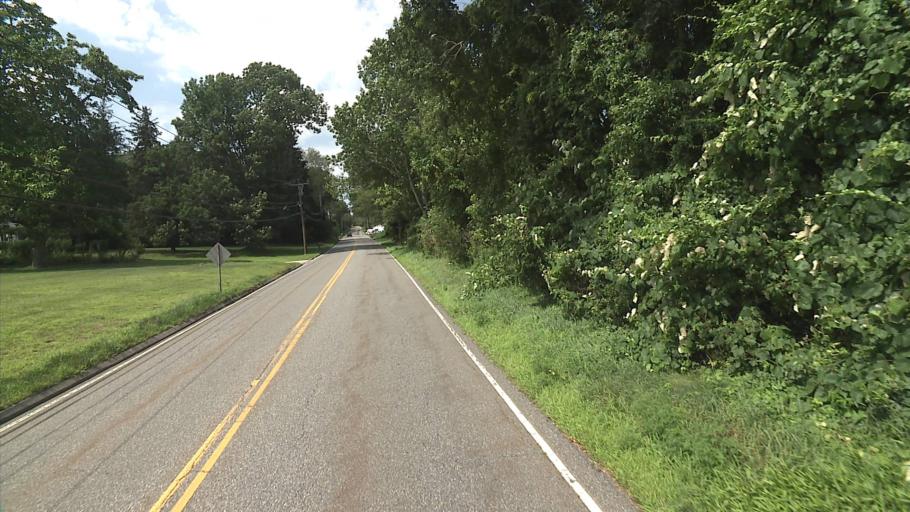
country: US
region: Connecticut
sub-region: New London County
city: Montville Center
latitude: 41.5108
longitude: -72.2488
